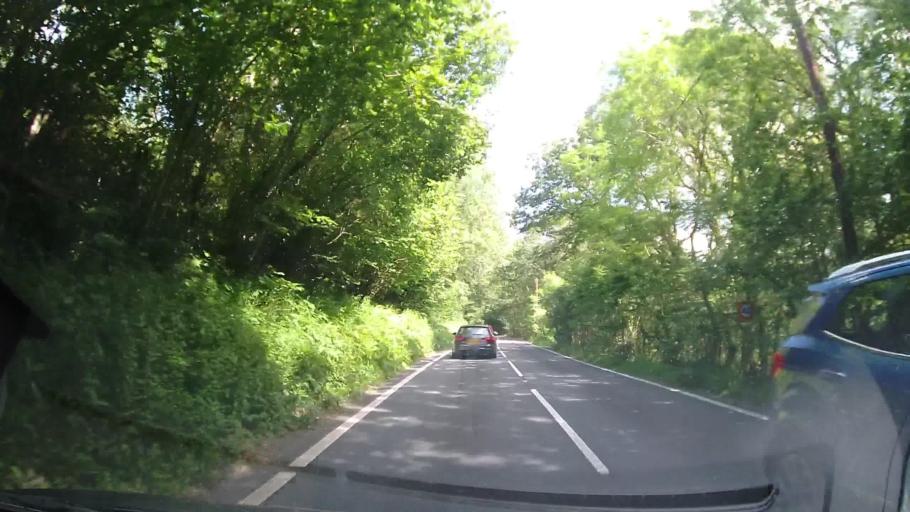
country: GB
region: Wales
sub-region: Gwynedd
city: Corris
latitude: 52.7040
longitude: -3.6670
